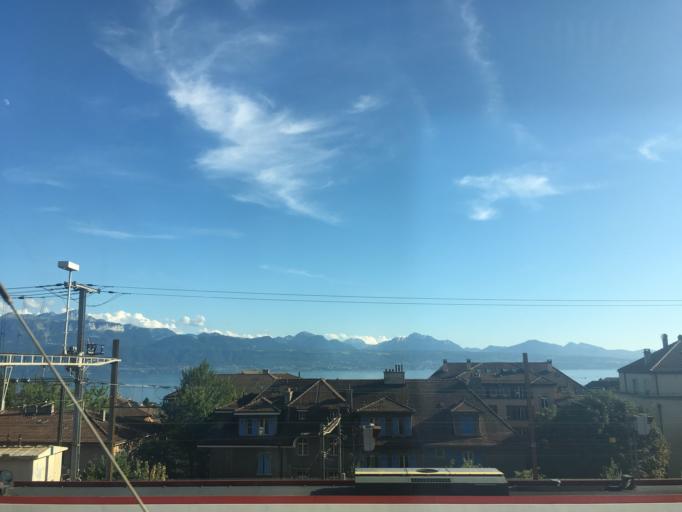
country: CH
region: Vaud
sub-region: Lausanne District
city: Lausanne
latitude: 46.5133
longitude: 6.6386
